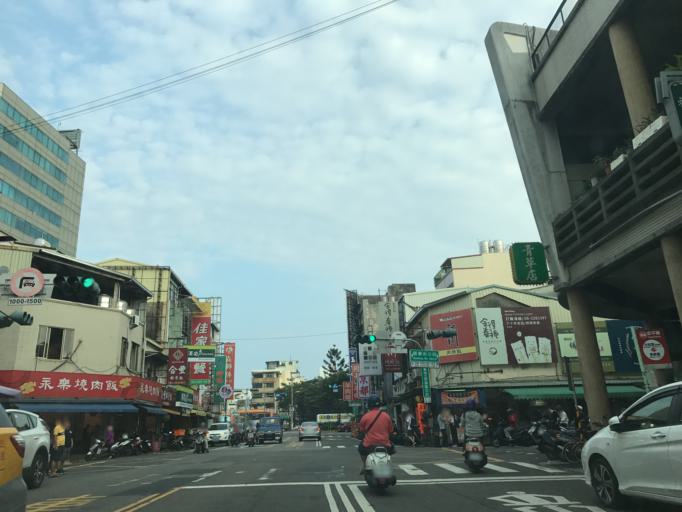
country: TW
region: Taiwan
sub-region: Tainan
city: Tainan
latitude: 22.9978
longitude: 120.1988
